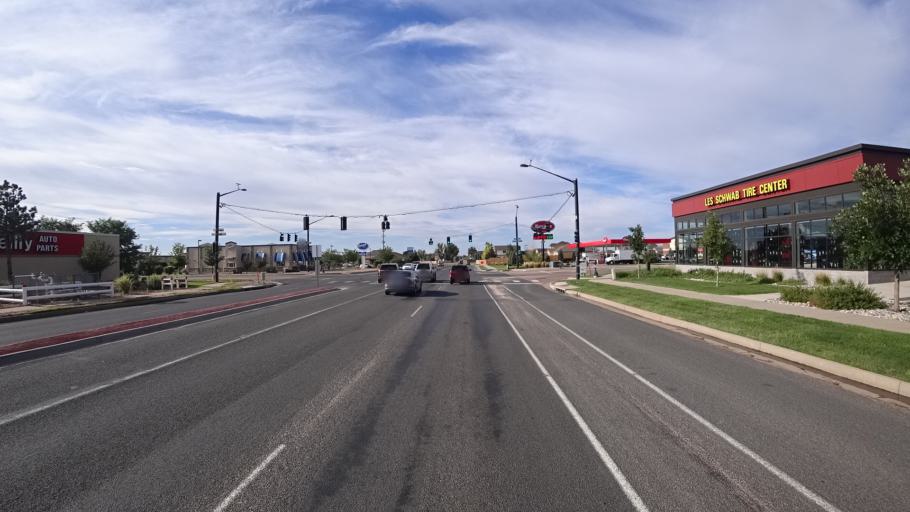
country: US
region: Colorado
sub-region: El Paso County
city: Security-Widefield
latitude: 38.7161
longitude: -104.7016
